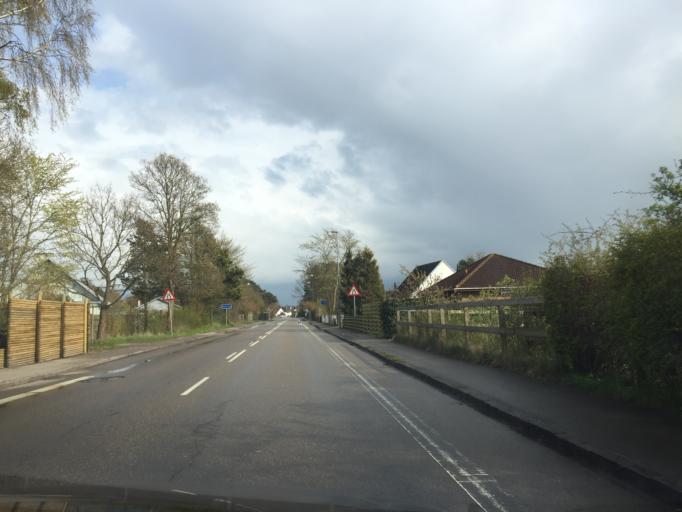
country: DK
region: Capital Region
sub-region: Halsnaes Kommune
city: Liseleje
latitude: 56.0092
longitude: 11.9816
